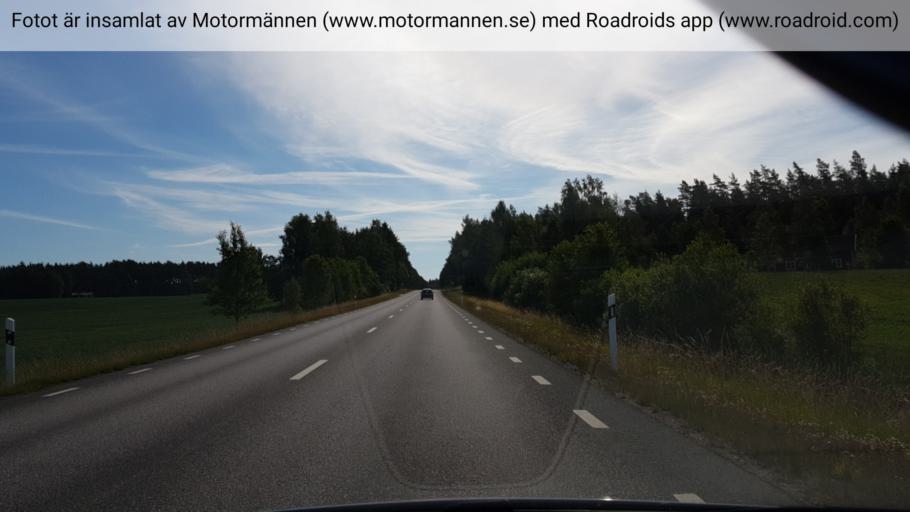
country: SE
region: Vaestra Goetaland
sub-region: Tibro Kommun
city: Tibro
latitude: 58.3414
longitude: 14.1995
